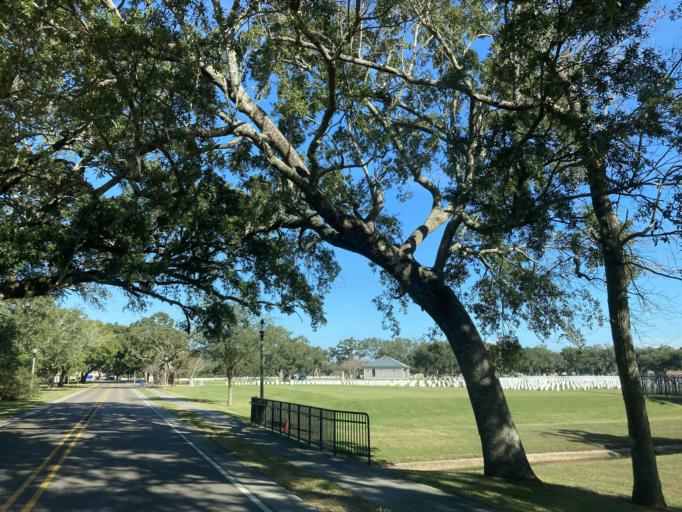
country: US
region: Mississippi
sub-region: Harrison County
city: D'Iberville
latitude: 30.4079
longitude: -88.9472
